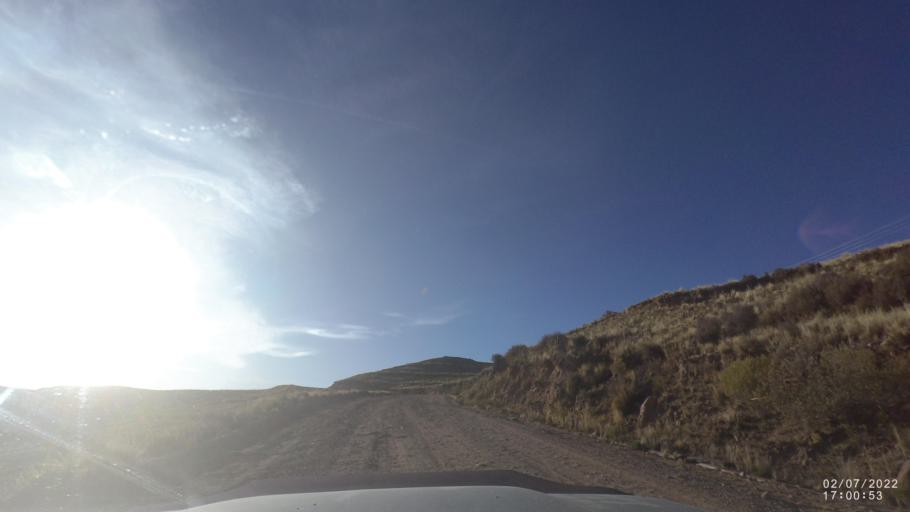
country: BO
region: Cochabamba
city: Irpa Irpa
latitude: -17.9351
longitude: -66.5547
